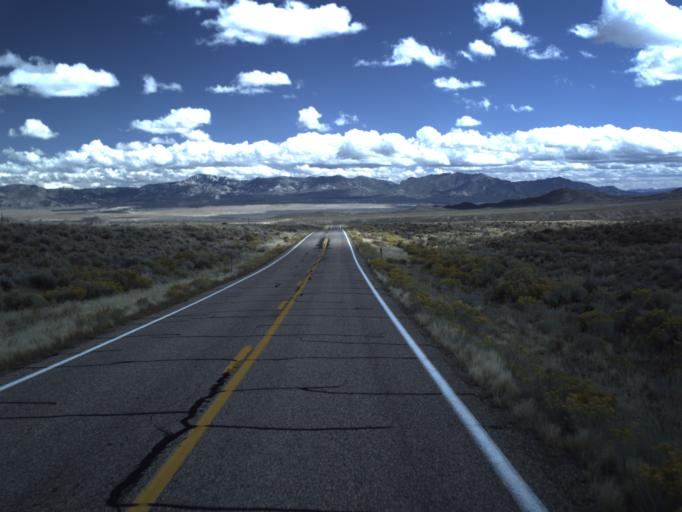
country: US
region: Utah
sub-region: Beaver County
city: Milford
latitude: 38.4462
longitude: -113.1842
